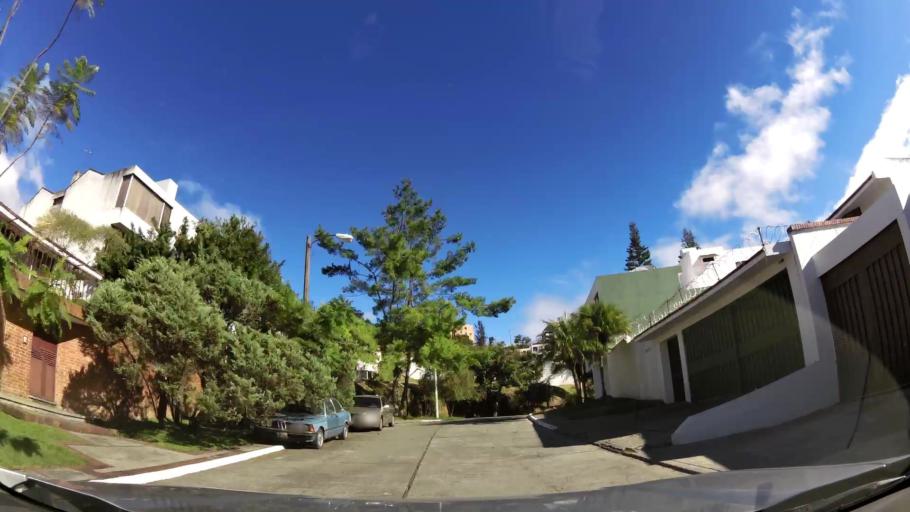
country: GT
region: Guatemala
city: Santa Catarina Pinula
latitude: 14.5678
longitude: -90.5274
